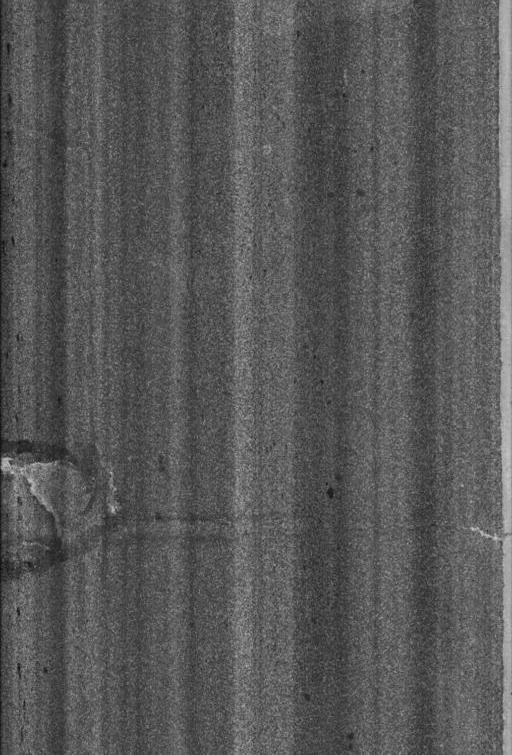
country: US
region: Maryland
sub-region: Prince George's County
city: Glassmanor
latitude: 38.8356
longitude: -77.0120
